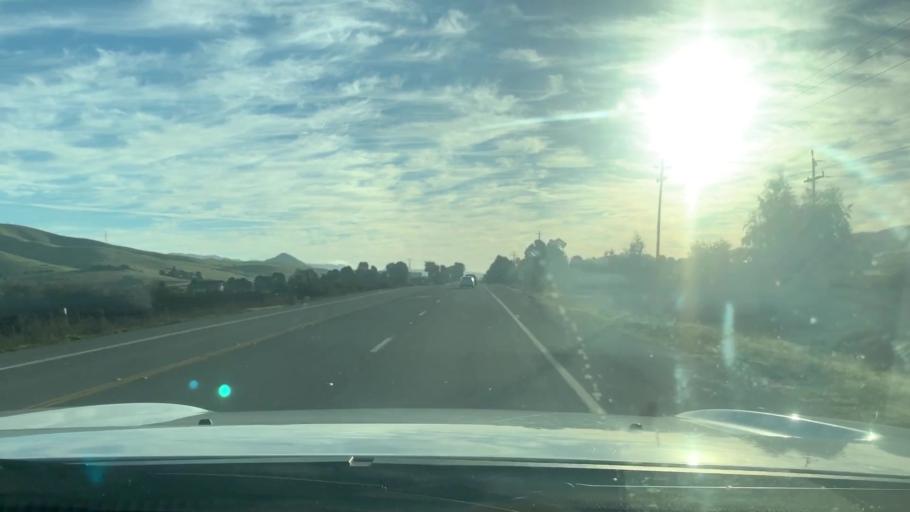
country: US
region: California
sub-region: San Luis Obispo County
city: Los Osos
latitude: 35.2952
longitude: -120.7626
